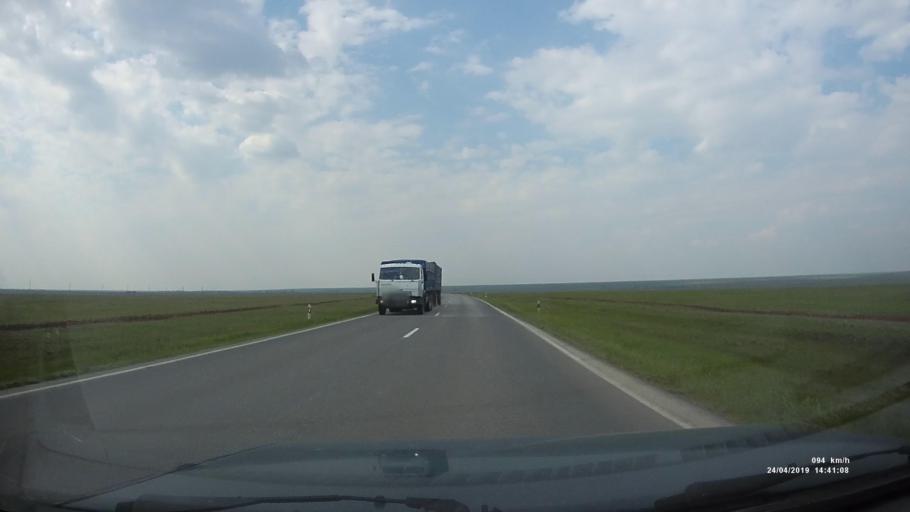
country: RU
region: Rostov
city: Remontnoye
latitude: 46.4416
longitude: 43.8832
